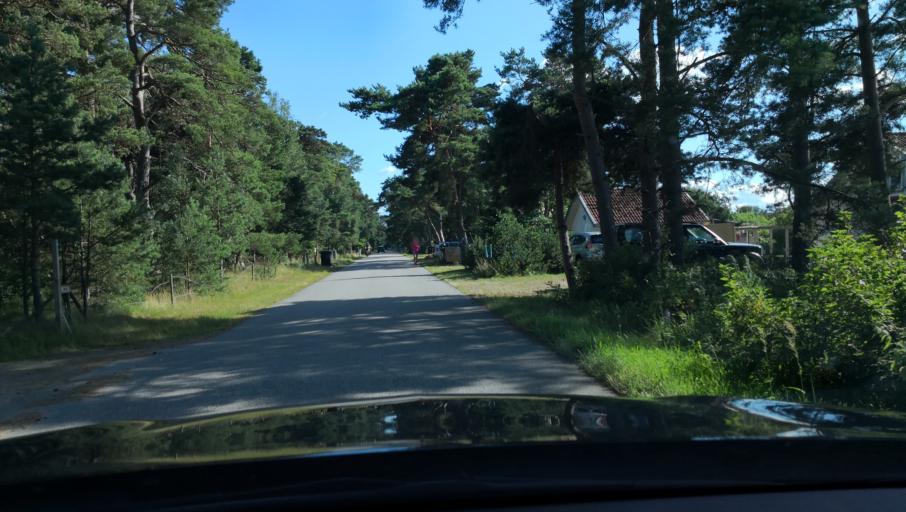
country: SE
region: Skane
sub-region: Simrishamns Kommun
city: Kivik
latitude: 55.7721
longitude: 14.1965
